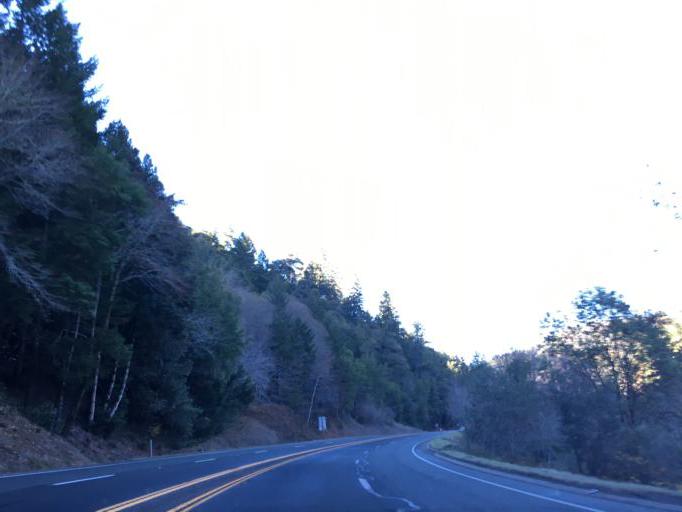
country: US
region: California
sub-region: Mendocino County
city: Brooktrails
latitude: 39.5443
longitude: -123.4238
